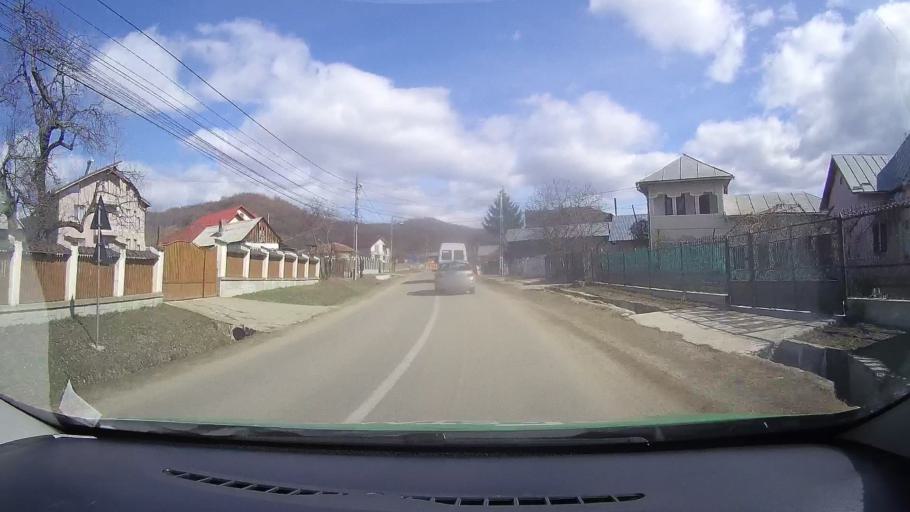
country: RO
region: Dambovita
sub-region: Comuna Glodeni
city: Laculete
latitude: 45.0205
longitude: 25.4488
